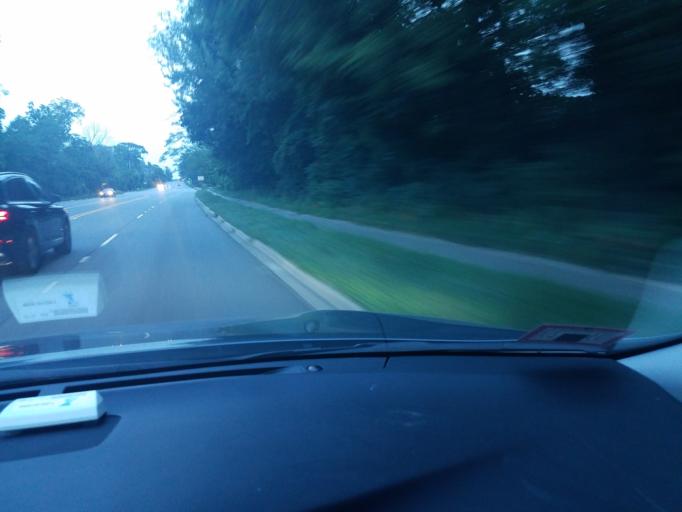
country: US
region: Illinois
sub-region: Cook County
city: Northbrook
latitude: 42.1380
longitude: -87.8112
